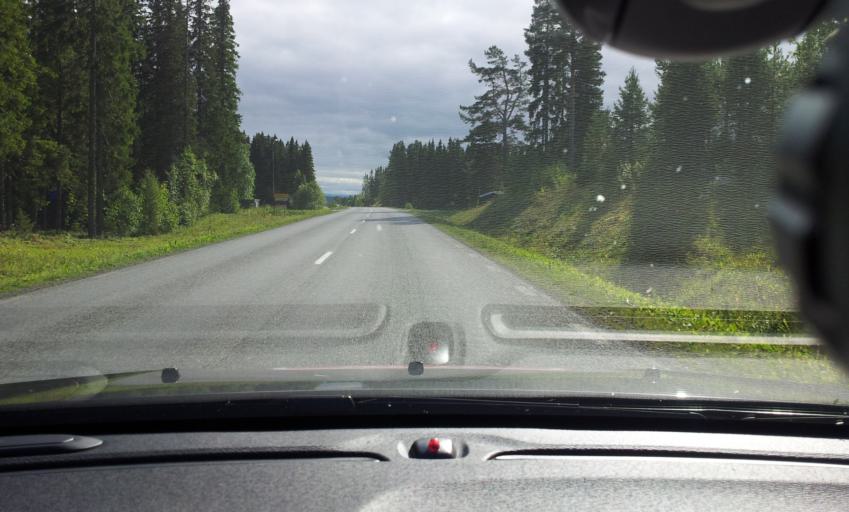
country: SE
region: Jaemtland
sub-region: Krokoms Kommun
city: Krokom
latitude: 63.4623
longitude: 14.1916
